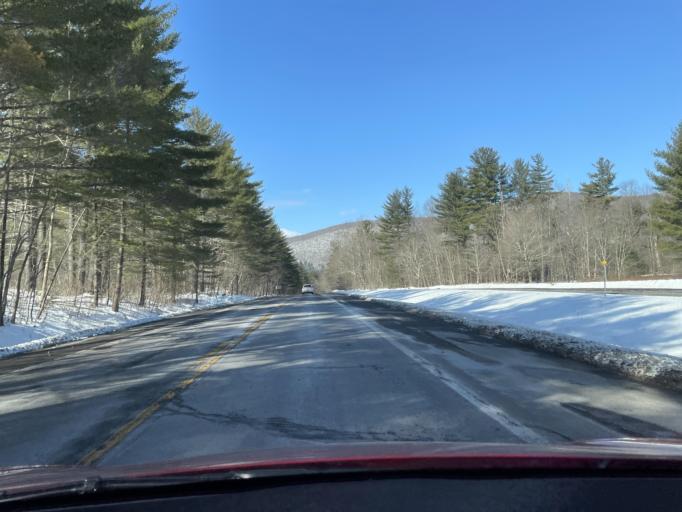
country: US
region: New York
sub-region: Ulster County
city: Shokan
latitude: 42.1155
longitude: -74.4124
